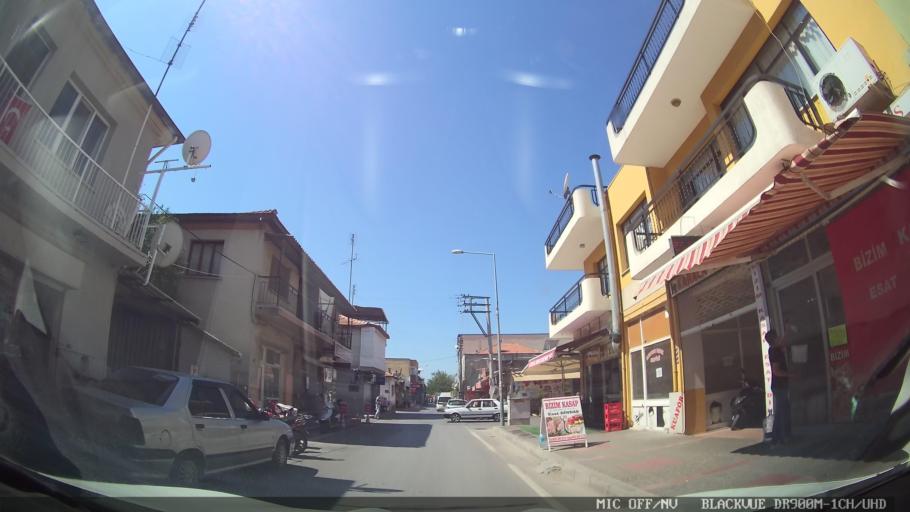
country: TR
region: Izmir
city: Karsiyaka
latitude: 38.4958
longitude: 27.0644
